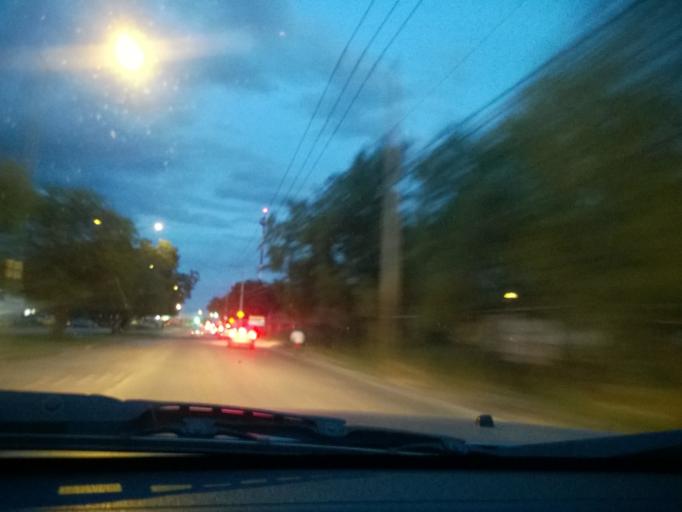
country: MX
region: Guanajuato
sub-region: Leon
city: Fraccionamiento Paraiso Real
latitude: 21.1121
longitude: -101.6043
